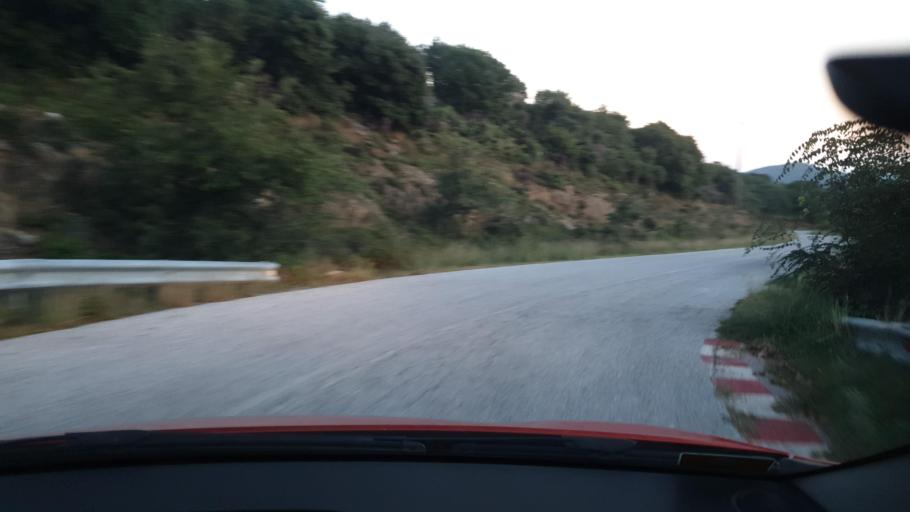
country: GR
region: Central Macedonia
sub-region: Nomos Thessalonikis
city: Peristera
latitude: 40.5235
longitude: 23.1890
